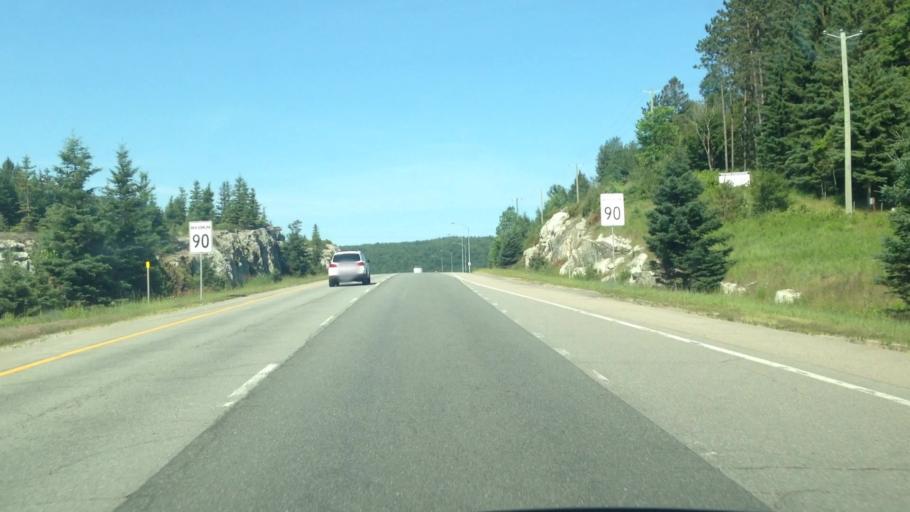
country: CA
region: Quebec
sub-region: Laurentides
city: Mont-Tremblant
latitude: 46.1153
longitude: -74.5830
